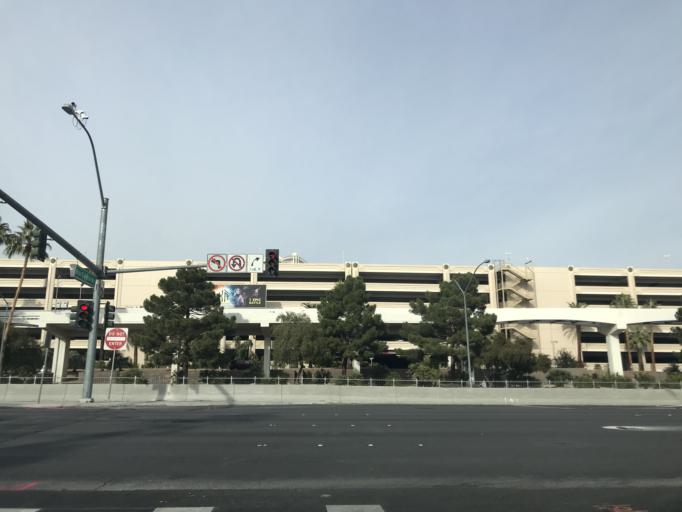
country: US
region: Nevada
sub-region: Clark County
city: Paradise
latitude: 36.1007
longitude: -115.1666
